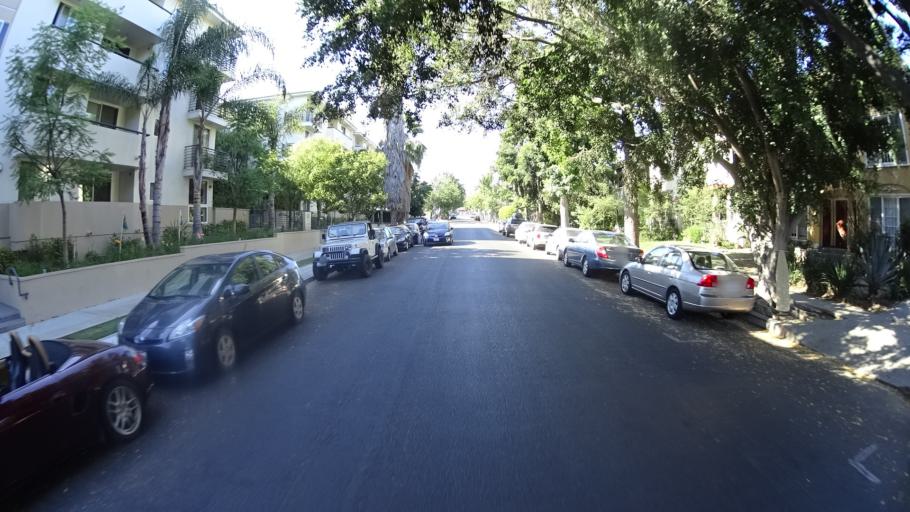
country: US
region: California
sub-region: Los Angeles County
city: West Hollywood
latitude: 34.0866
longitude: -118.3638
